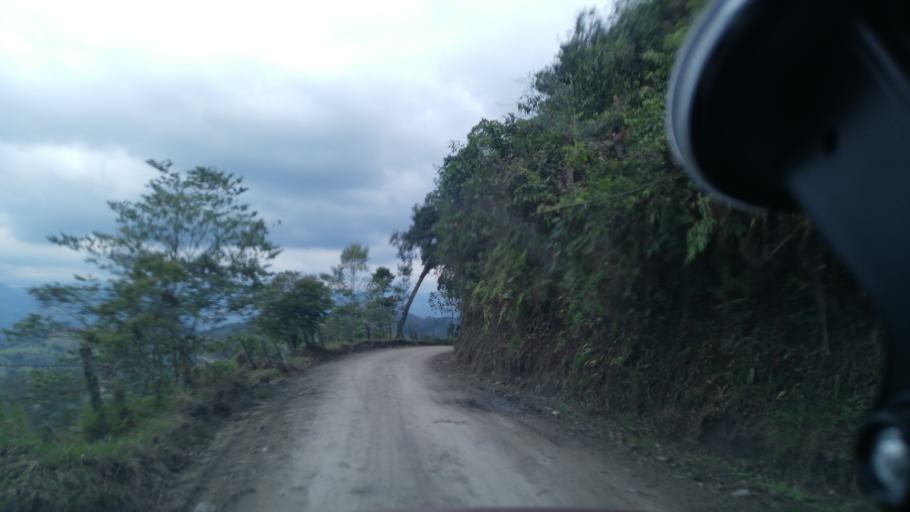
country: CO
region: Cundinamarca
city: Vergara
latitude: 5.1595
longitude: -74.2569
